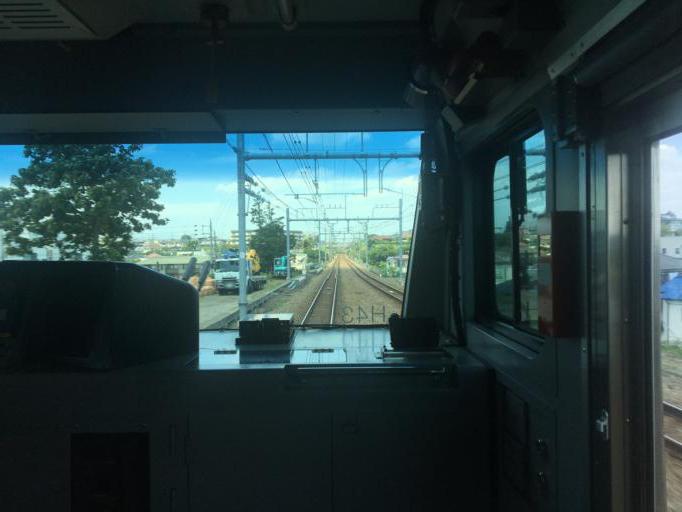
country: JP
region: Tokyo
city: Hino
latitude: 35.6894
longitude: 139.3992
